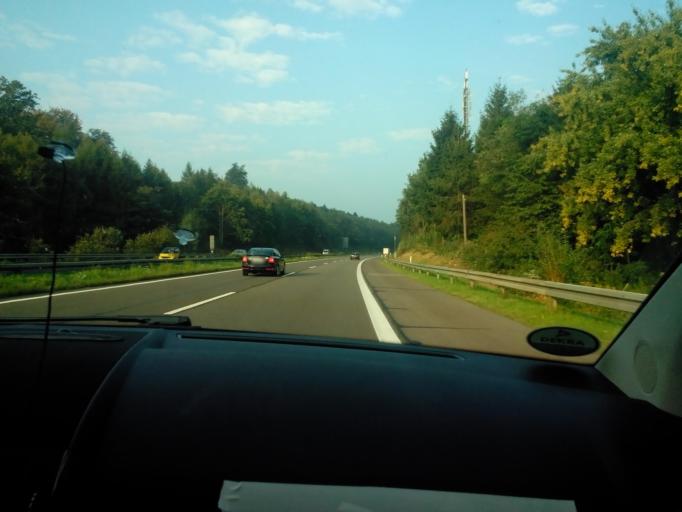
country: DE
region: Saarland
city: Puttlingen
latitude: 49.3195
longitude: 6.8650
